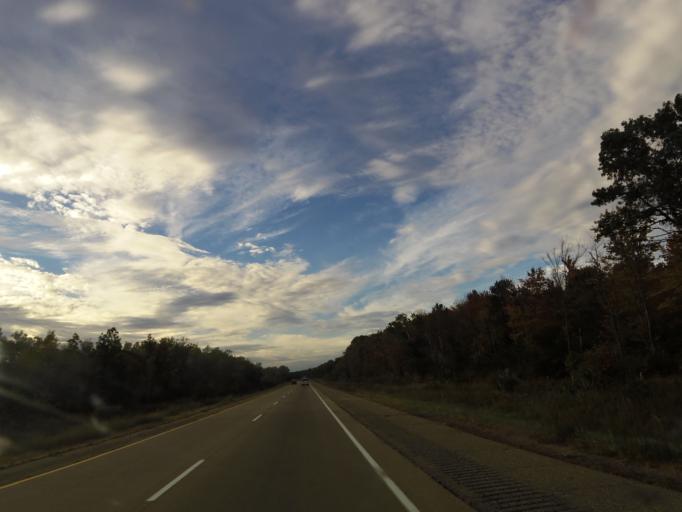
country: US
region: Wisconsin
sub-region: Columbia County
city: Wisconsin Dells
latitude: 43.6852
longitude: -89.8414
